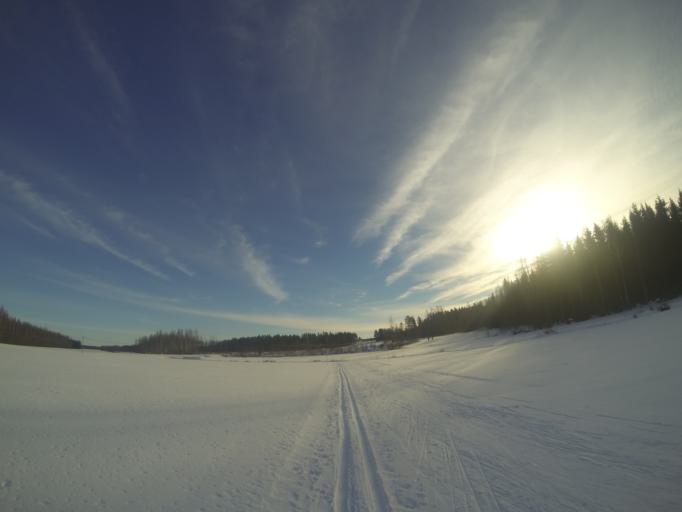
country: FI
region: Southern Savonia
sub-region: Savonlinna
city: Savonlinna
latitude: 61.9430
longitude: 28.9184
